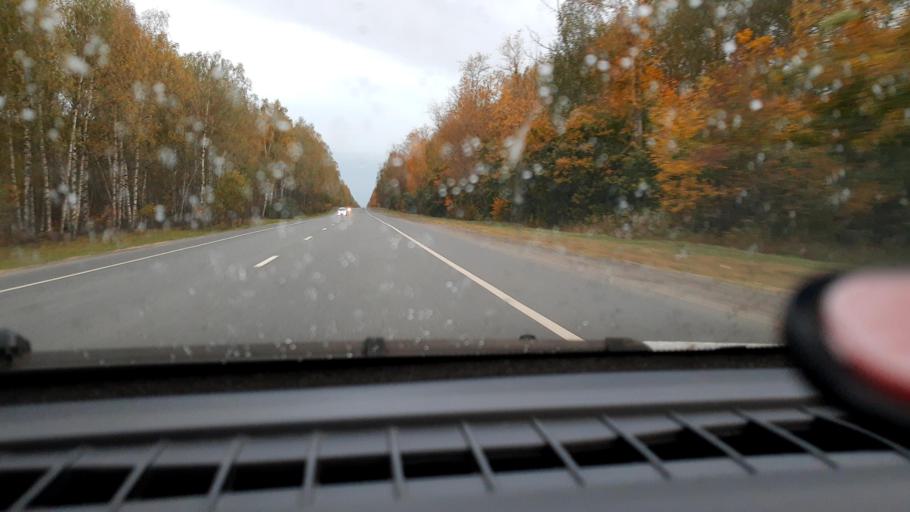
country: RU
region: Vladimir
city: Orgtrud
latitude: 56.2038
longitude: 40.7473
